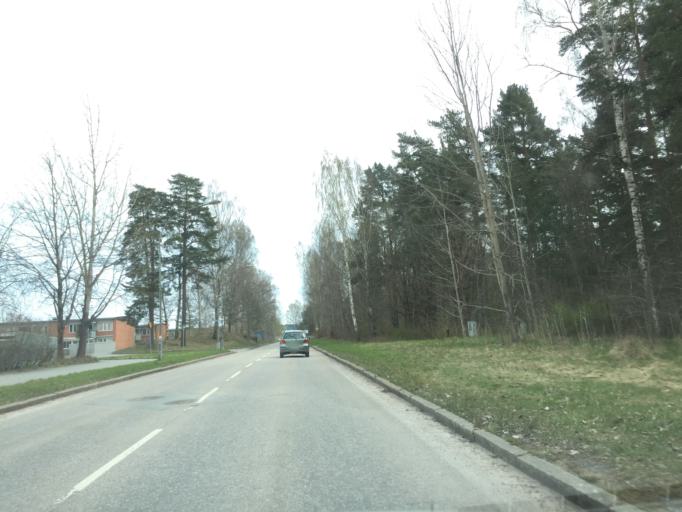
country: SE
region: OErebro
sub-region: Orebro Kommun
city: Orebro
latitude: 59.2946
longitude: 15.1903
